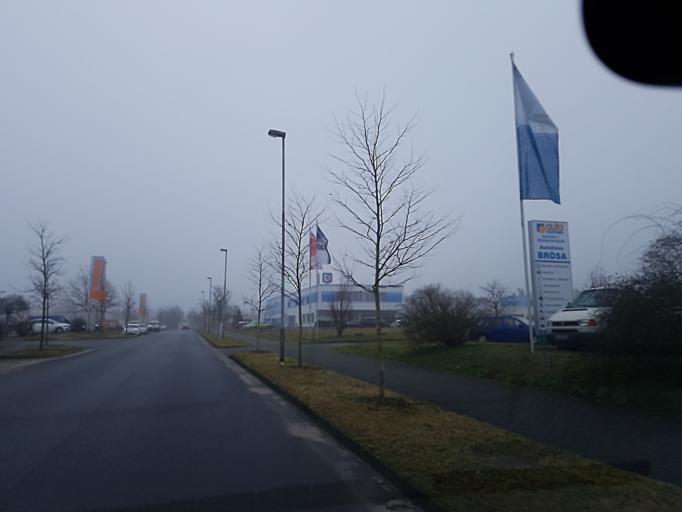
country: DE
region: Brandenburg
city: Finsterwalde
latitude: 51.6351
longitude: 13.7358
